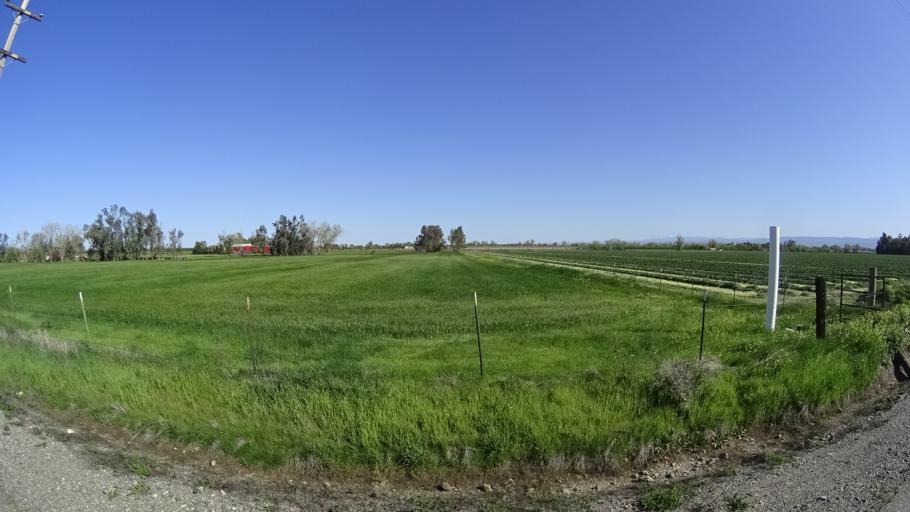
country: US
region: California
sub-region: Glenn County
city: Hamilton City
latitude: 39.7753
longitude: -122.0624
